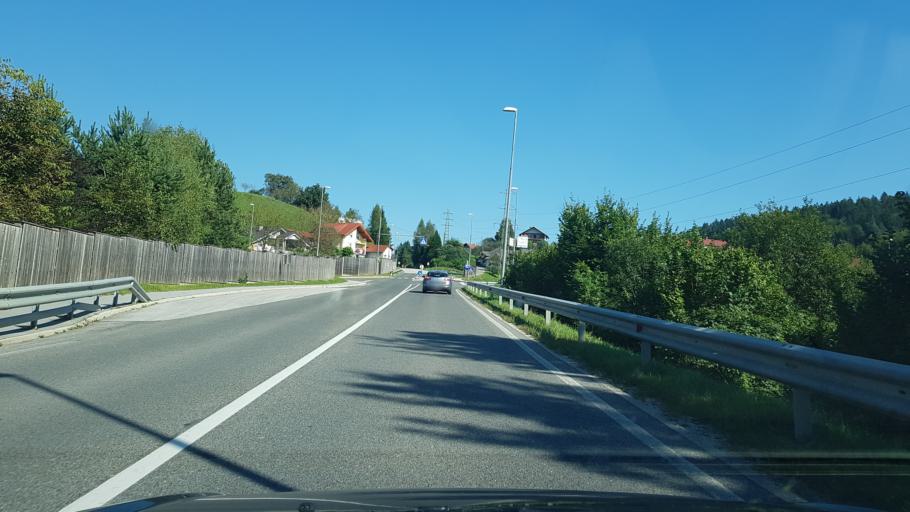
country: SI
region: Sostanj
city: Sostanj
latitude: 46.3629
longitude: 15.0561
